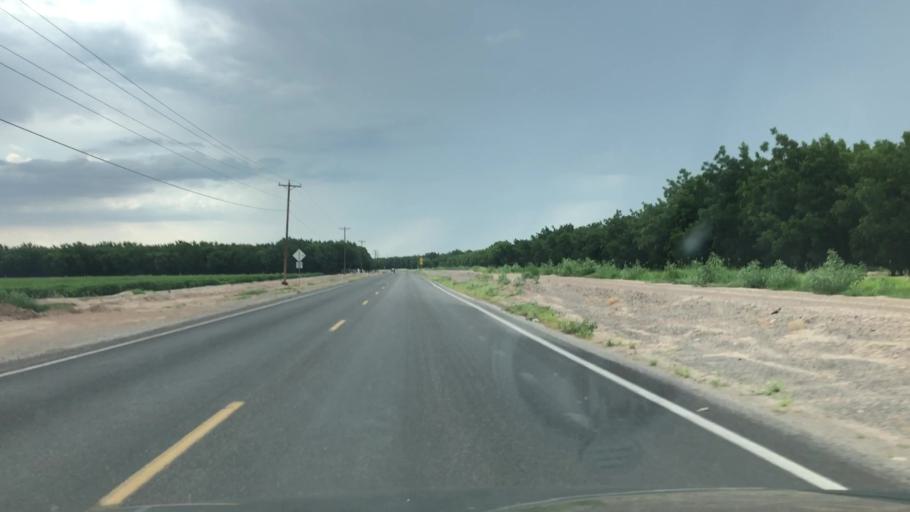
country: US
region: New Mexico
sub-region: Dona Ana County
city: La Union
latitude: 31.9874
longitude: -106.6500
